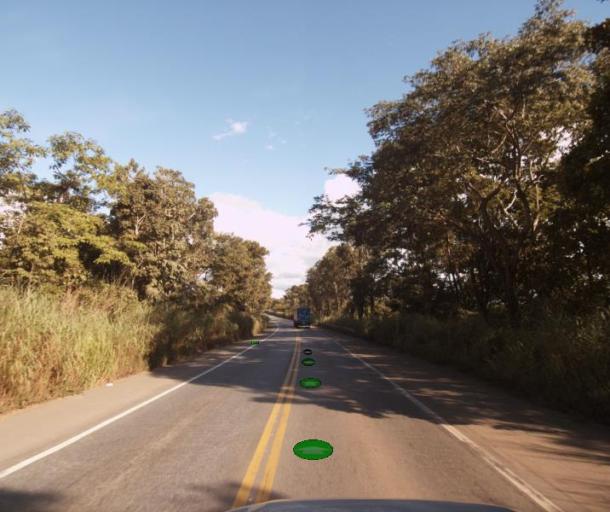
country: BR
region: Goias
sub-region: Porangatu
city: Porangatu
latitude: -13.1152
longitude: -49.2019
